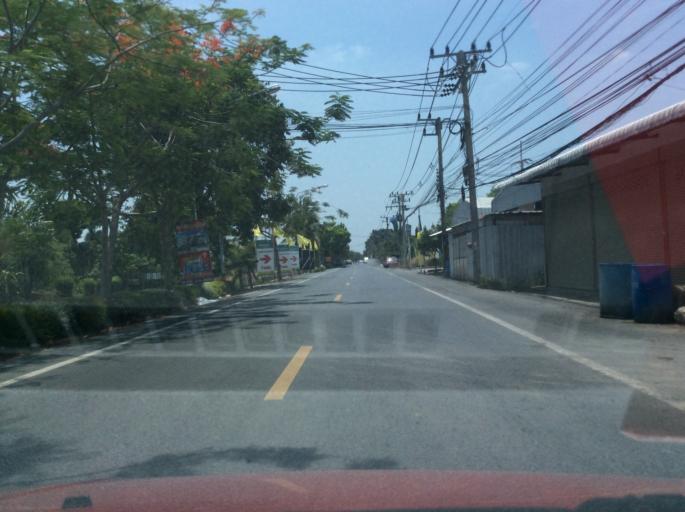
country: TH
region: Pathum Thani
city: Lam Luk Ka
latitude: 13.9609
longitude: 100.7277
